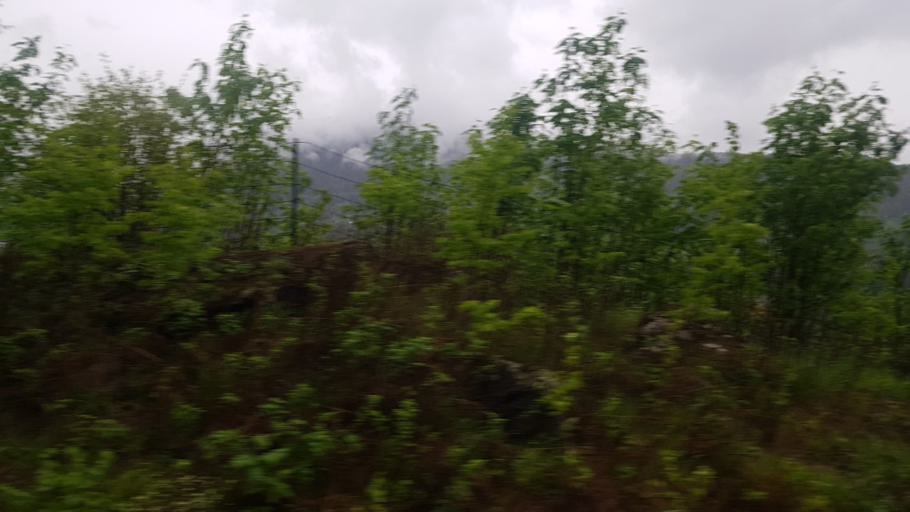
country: NO
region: Oppland
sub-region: Oyer
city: Tretten
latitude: 61.4214
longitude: 10.2301
